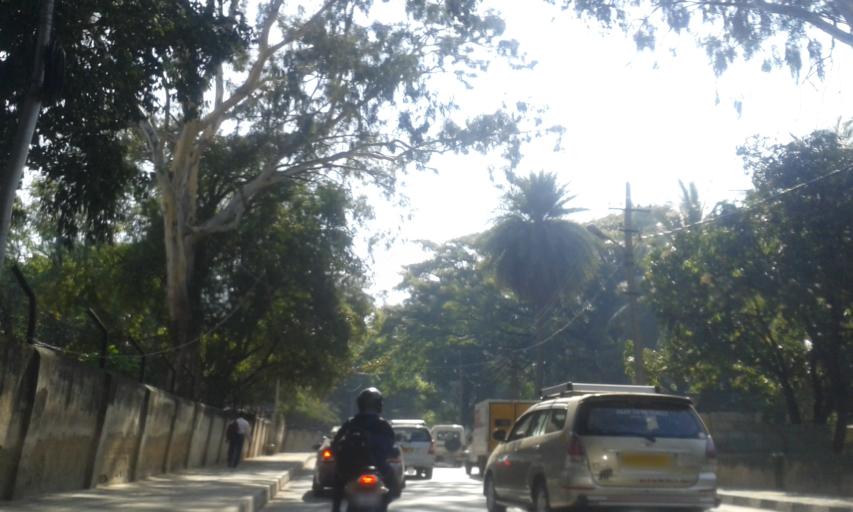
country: IN
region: Karnataka
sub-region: Bangalore Urban
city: Bangalore
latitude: 12.9669
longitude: 77.6162
